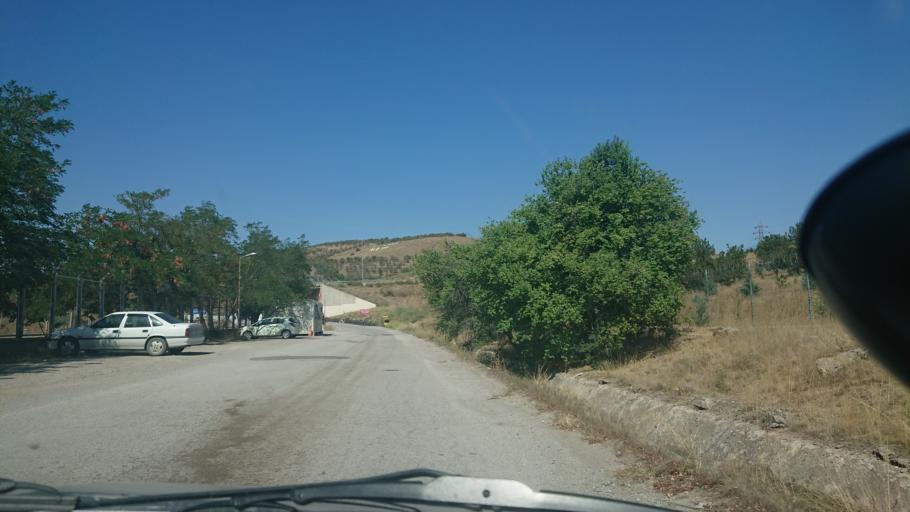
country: TR
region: Ankara
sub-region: Goelbasi
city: Golbasi
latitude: 39.8111
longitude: 32.8214
